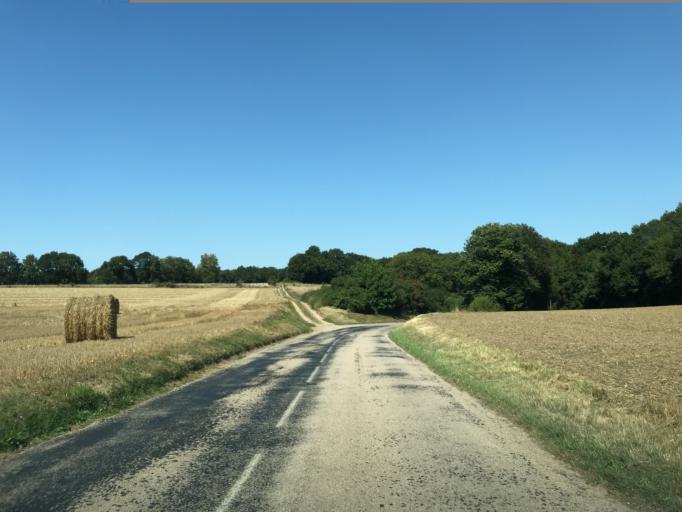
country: FR
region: Haute-Normandie
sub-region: Departement de l'Eure
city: Heudreville-sur-Eure
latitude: 49.1023
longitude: 1.2043
